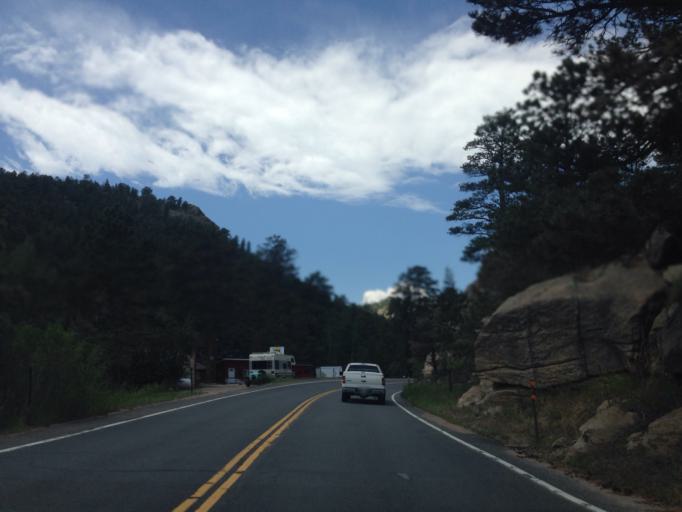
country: US
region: Colorado
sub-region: Larimer County
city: Estes Park
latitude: 40.3911
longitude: -105.4568
